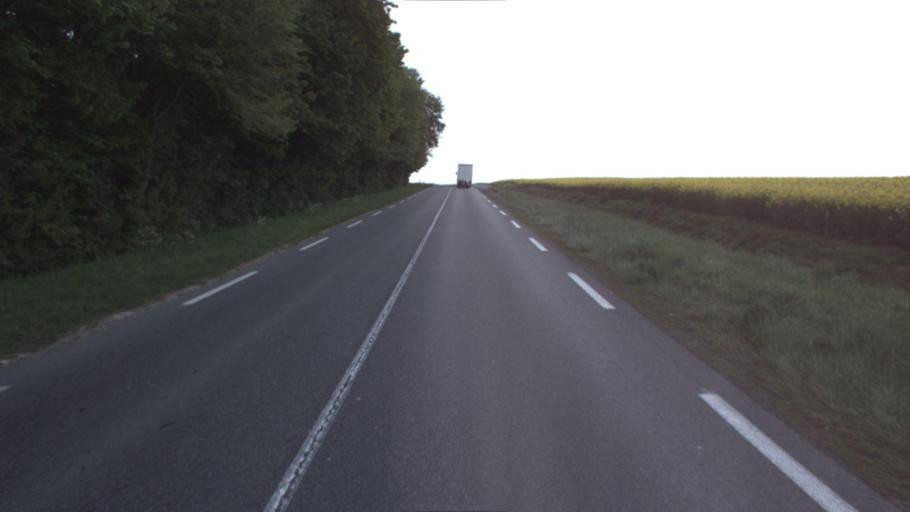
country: FR
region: Ile-de-France
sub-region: Departement de Seine-et-Marne
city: Villiers-Saint-Georges
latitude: 48.6922
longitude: 3.3276
